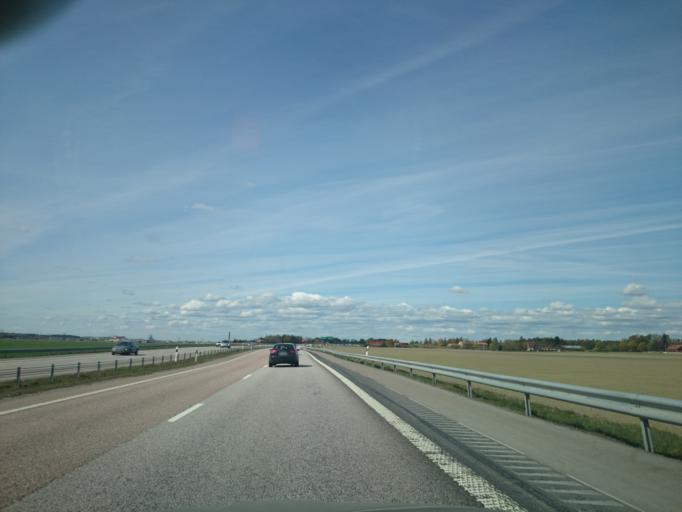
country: SE
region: Uppsala
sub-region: Uppsala Kommun
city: Saevja
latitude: 59.8248
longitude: 17.7453
